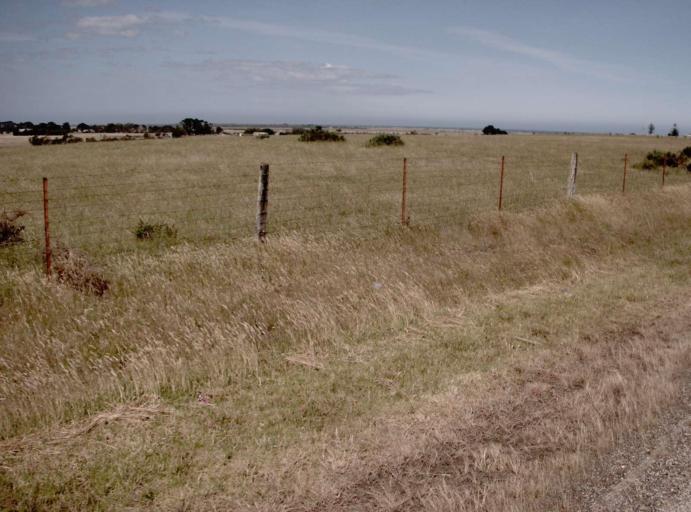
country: AU
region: Victoria
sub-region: Wellington
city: Sale
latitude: -38.3588
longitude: 147.1758
